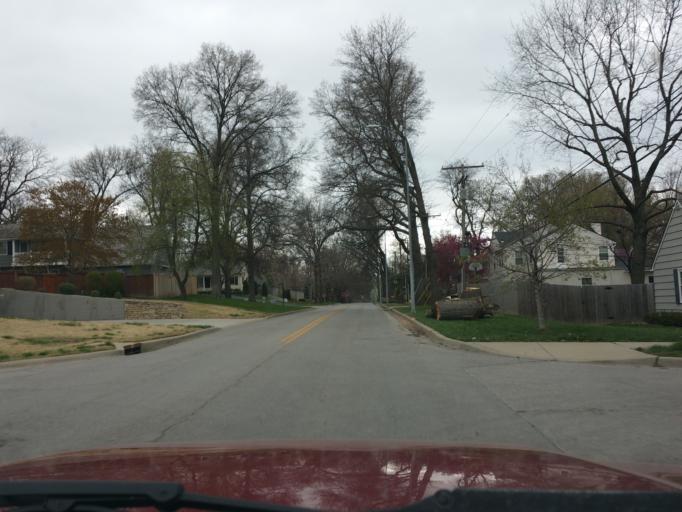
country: US
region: Kansas
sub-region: Johnson County
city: Mission Hills
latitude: 39.0043
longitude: -94.6079
